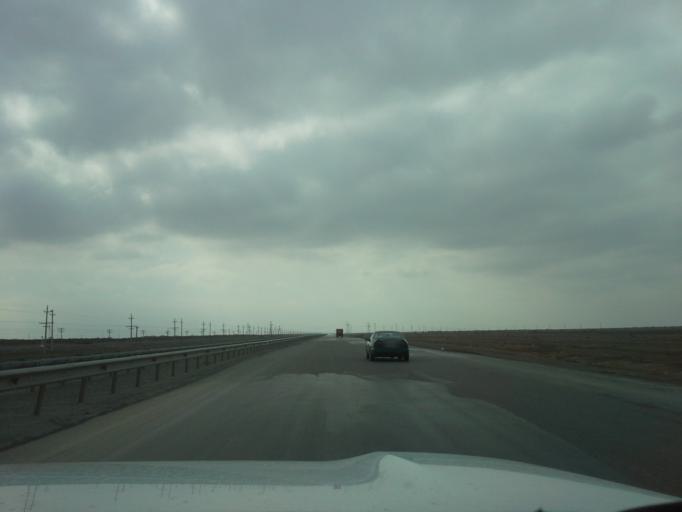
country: IR
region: Razavi Khorasan
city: Kalat-e Naderi
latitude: 37.2187
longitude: 60.1080
